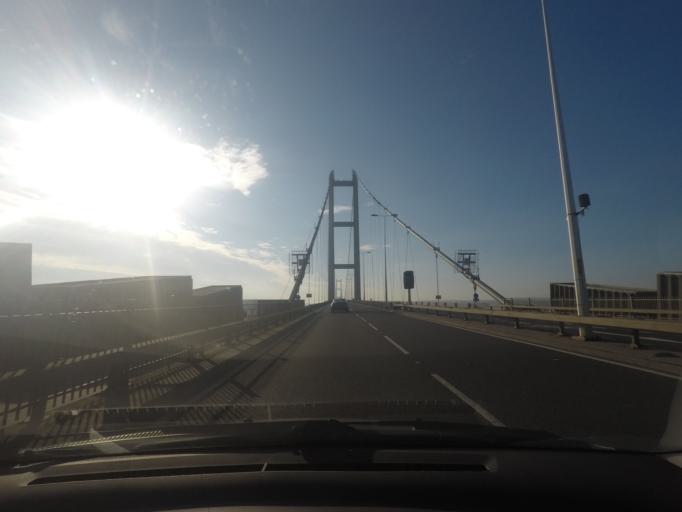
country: GB
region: England
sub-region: East Riding of Yorkshire
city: Hessle
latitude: 53.7172
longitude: -0.4507
